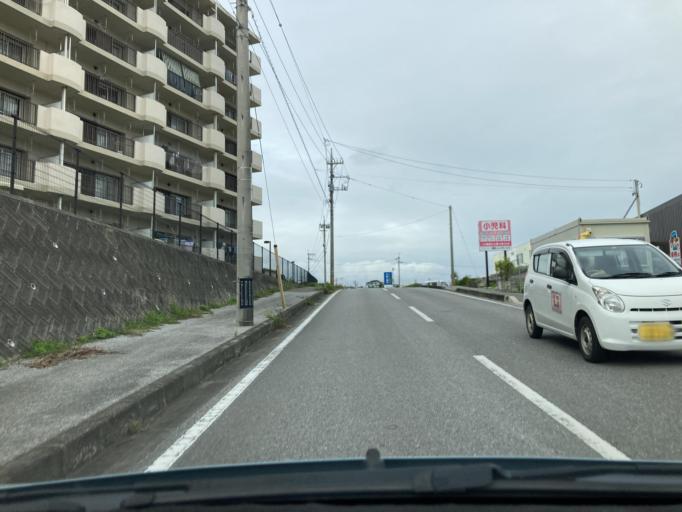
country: JP
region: Okinawa
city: Tomigusuku
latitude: 26.1517
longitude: 127.6968
